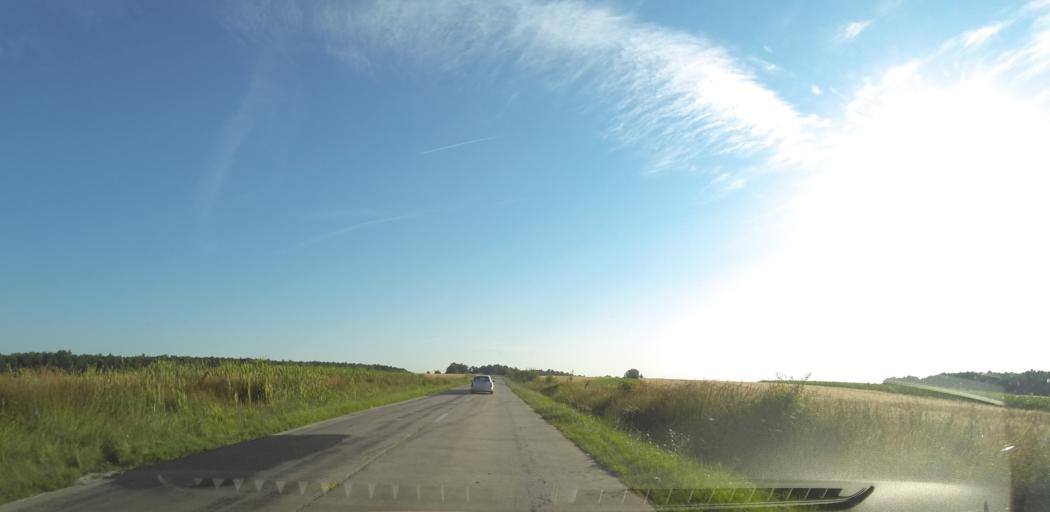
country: RO
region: Valcea
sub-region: Comuna Balcesti
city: Balcesti
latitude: 44.6008
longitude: 23.9285
